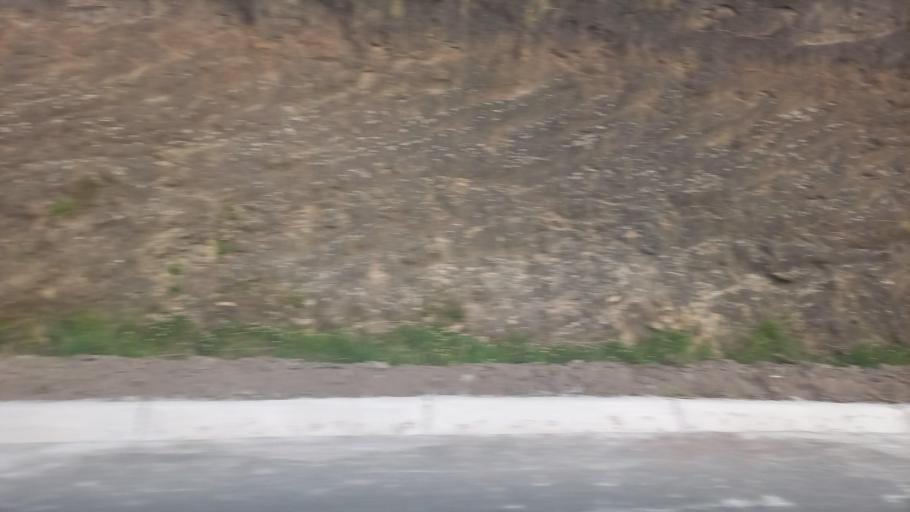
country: EC
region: Pichincha
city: Cayambe
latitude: 0.1231
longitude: -78.0756
